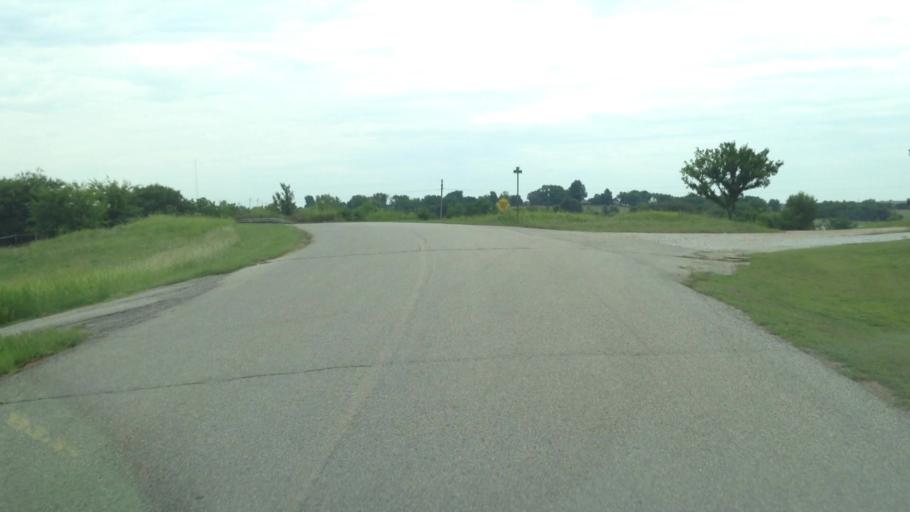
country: US
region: Oklahoma
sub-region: Craig County
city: Vinita
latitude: 36.6372
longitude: -95.1251
